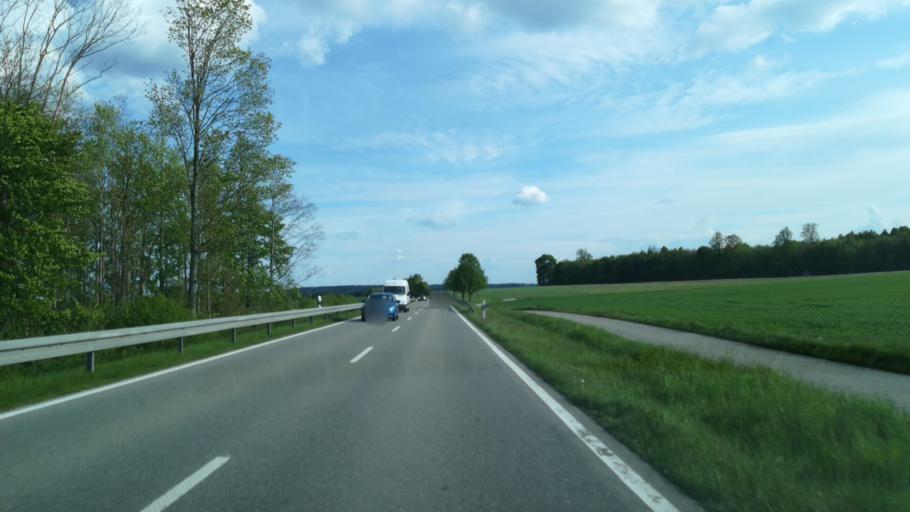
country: DE
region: Baden-Wuerttemberg
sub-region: Freiburg Region
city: Muhlingen
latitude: 47.9325
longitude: 9.0480
